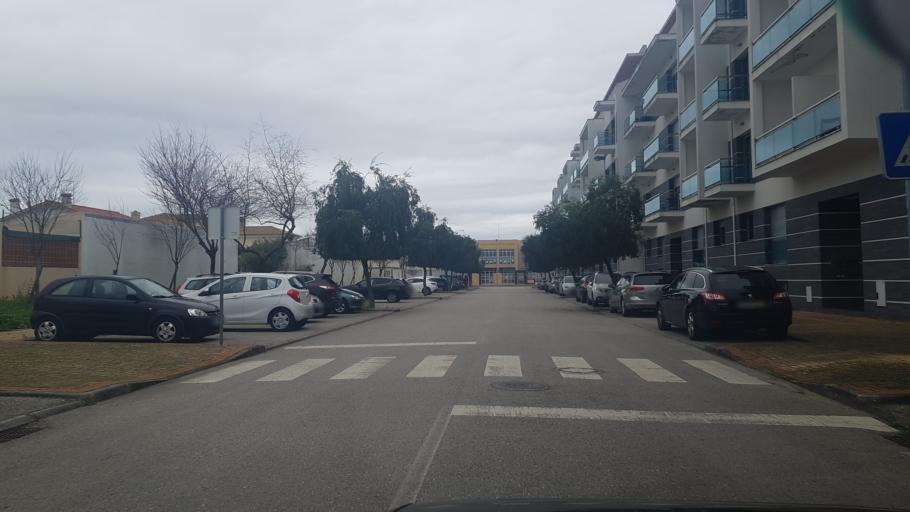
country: PT
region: Santarem
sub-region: Entroncamento
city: Entroncamento
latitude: 39.4552
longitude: -8.4717
